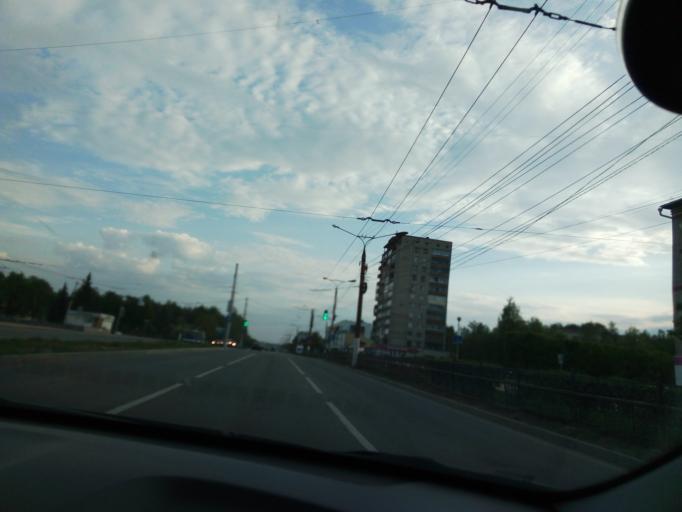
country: RU
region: Chuvashia
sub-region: Cheboksarskiy Rayon
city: Cheboksary
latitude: 56.1259
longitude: 47.2839
